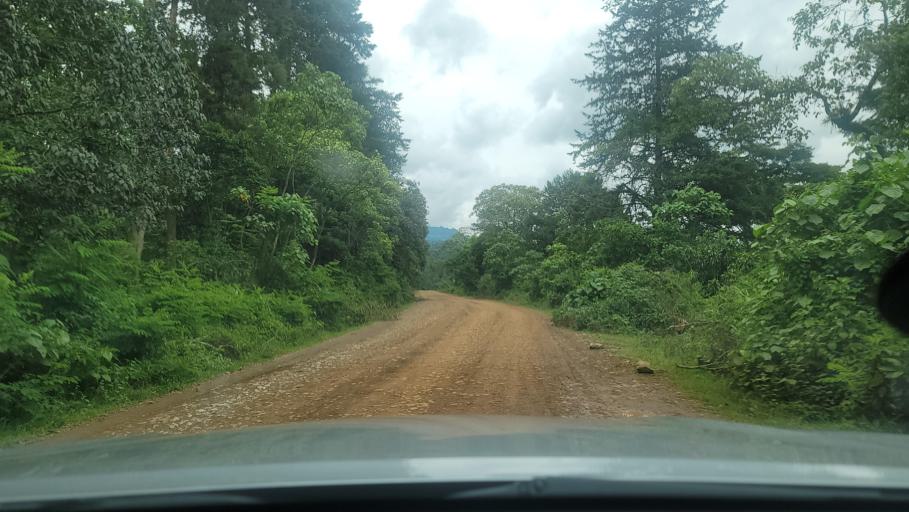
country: ET
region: Oromiya
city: Agaro
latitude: 7.7871
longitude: 36.4291
